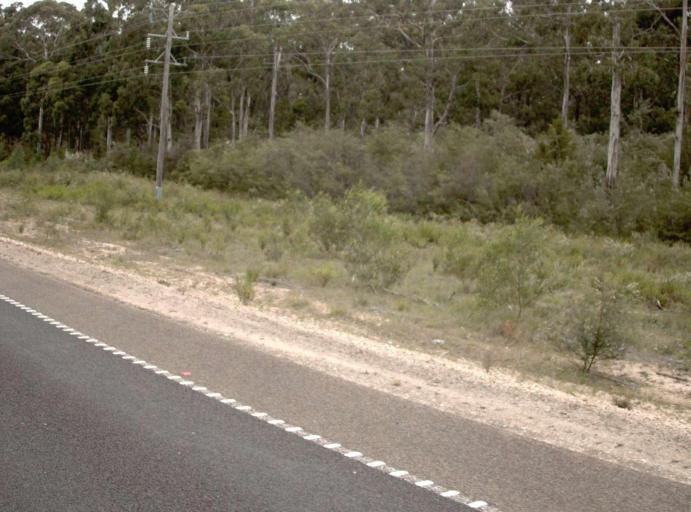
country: AU
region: Victoria
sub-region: East Gippsland
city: Lakes Entrance
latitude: -37.7113
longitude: 148.0725
